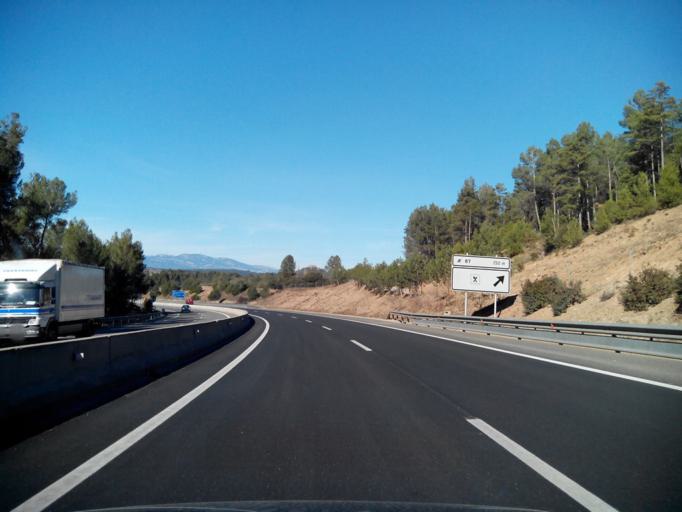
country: ES
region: Catalonia
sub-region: Provincia de Barcelona
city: Sallent
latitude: 41.8447
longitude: 1.8849
